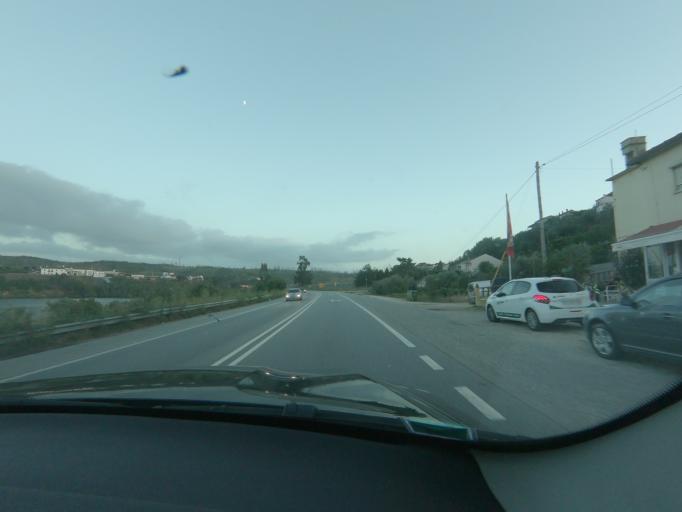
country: PT
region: Viseu
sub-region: Mortagua
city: Mortagua
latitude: 40.3243
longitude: -8.2304
